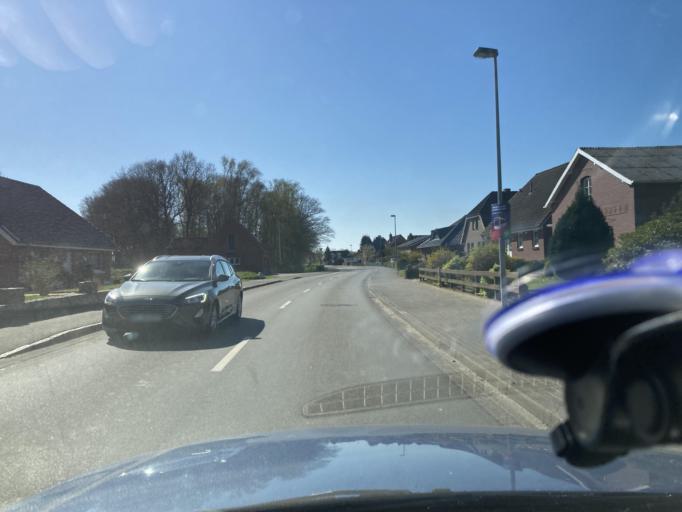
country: DE
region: Schleswig-Holstein
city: Sarzbuttel
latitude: 54.1162
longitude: 9.1850
